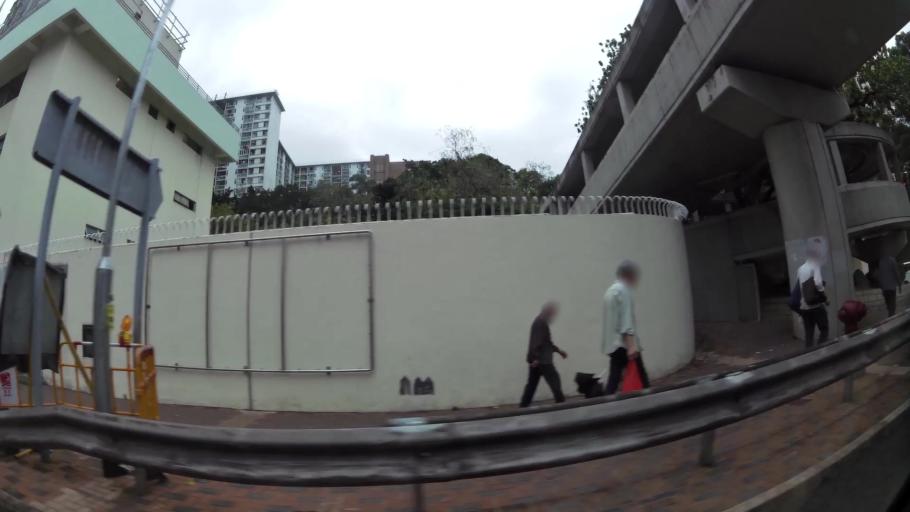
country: HK
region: Tsuen Wan
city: Tsuen Wan
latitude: 22.3738
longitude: 114.1219
